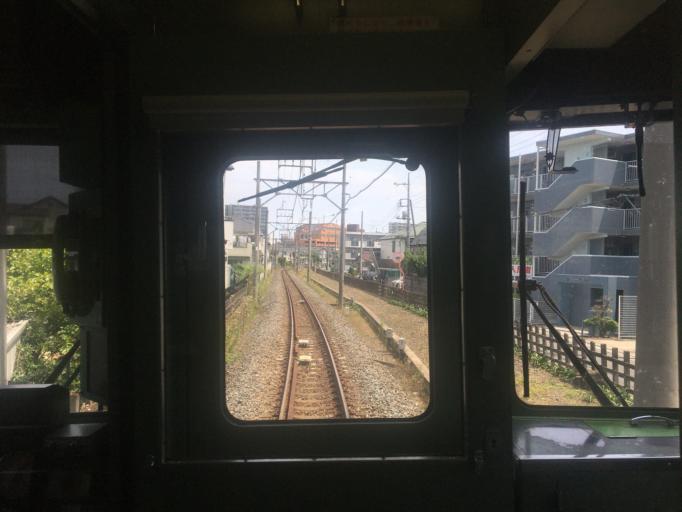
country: JP
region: Saitama
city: Sakado
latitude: 35.9543
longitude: 139.3897
